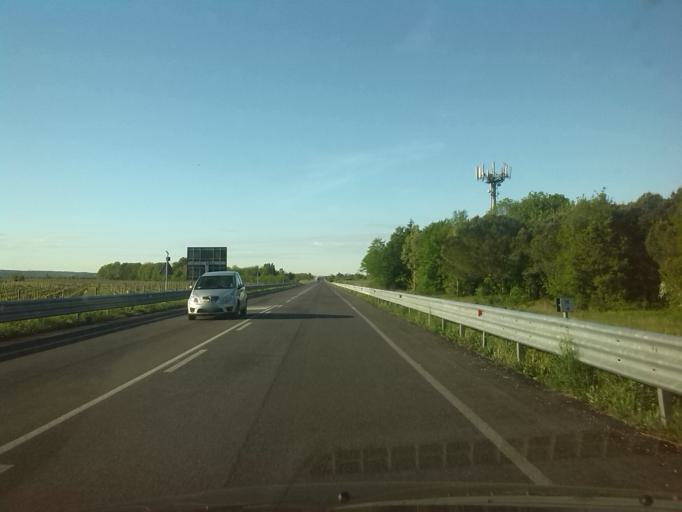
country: IT
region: Friuli Venezia Giulia
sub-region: Provincia di Gorizia
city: Mariano del Friuli
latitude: 45.9180
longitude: 13.4685
